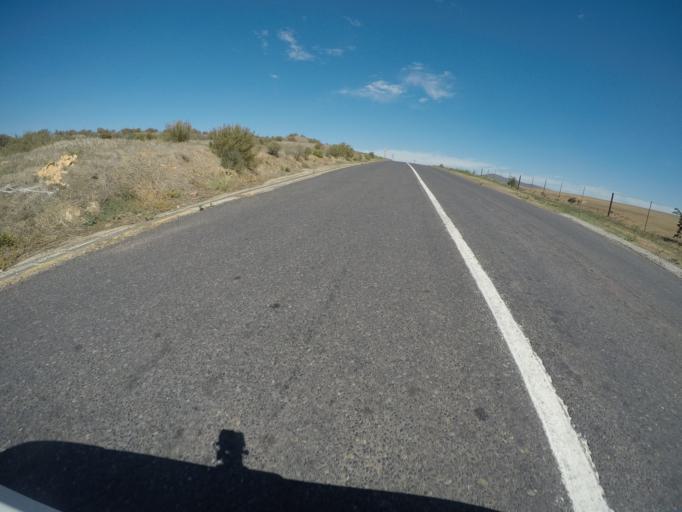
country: ZA
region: Western Cape
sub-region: City of Cape Town
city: Atlantis
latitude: -33.6788
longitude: 18.6041
